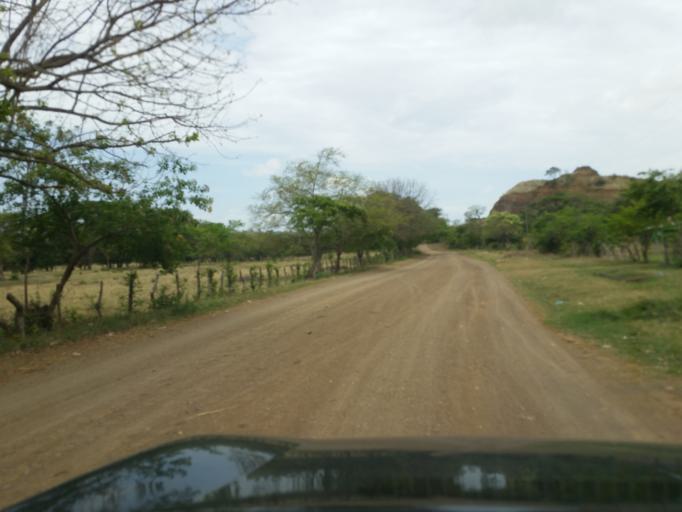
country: NI
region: Granada
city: Nandaime
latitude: 11.6445
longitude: -85.9991
